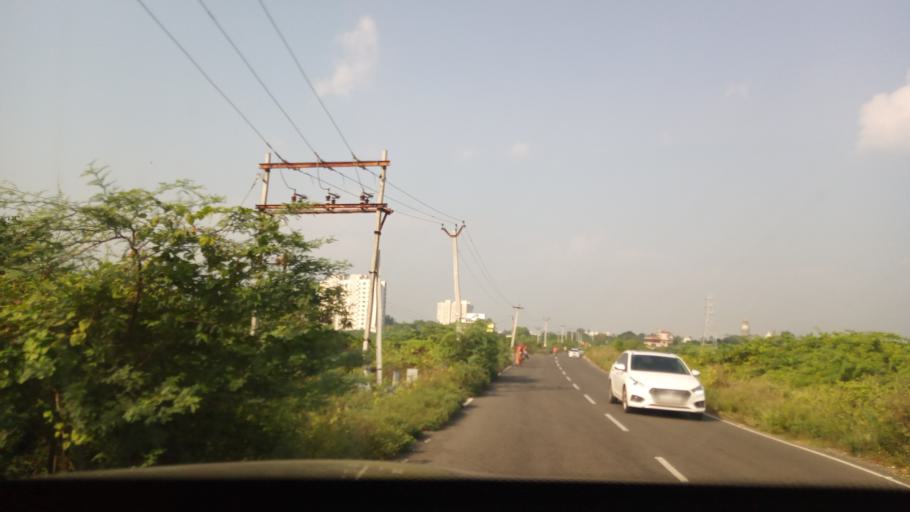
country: IN
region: Tamil Nadu
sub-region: Kancheepuram
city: Vengavasal
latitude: 12.7839
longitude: 80.2350
